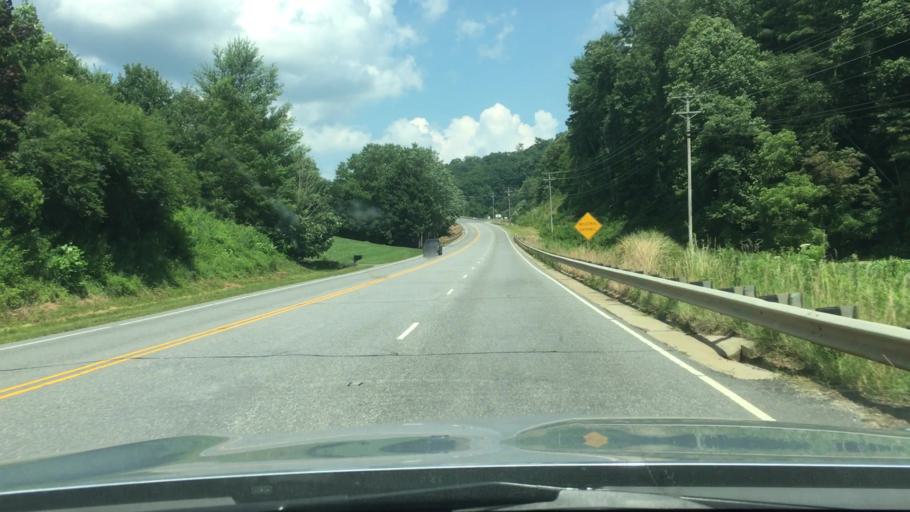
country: US
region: North Carolina
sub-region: Madison County
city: Marshall
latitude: 35.8191
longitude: -82.6458
